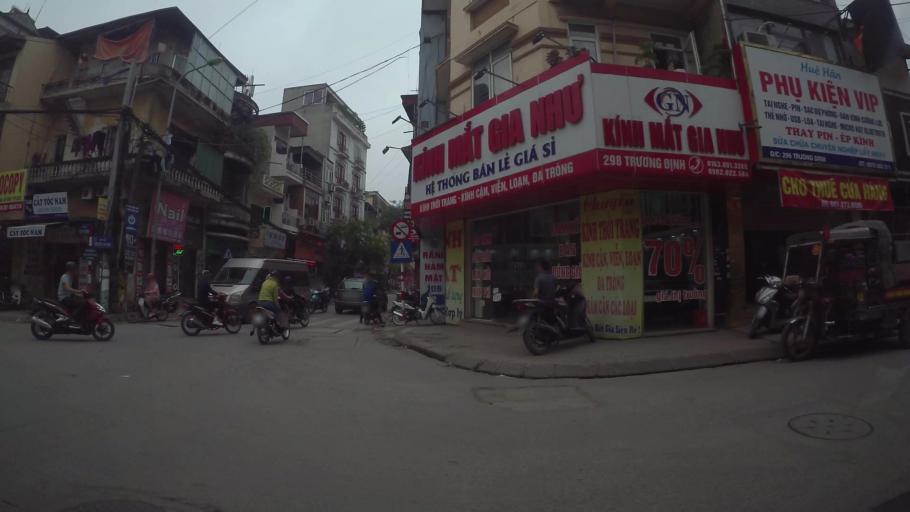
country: VN
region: Ha Noi
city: Hai BaTrung
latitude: 20.9888
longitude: 105.8471
